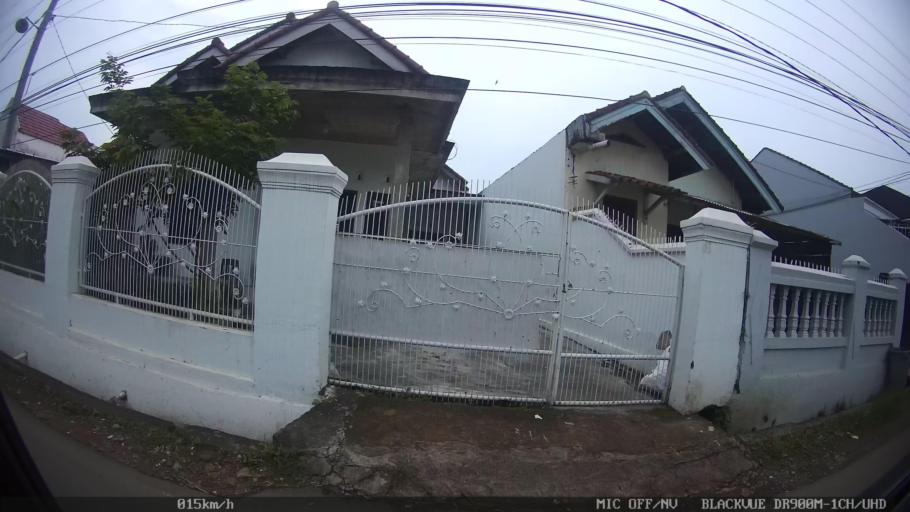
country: ID
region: Lampung
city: Kedaton
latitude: -5.3982
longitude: 105.2321
